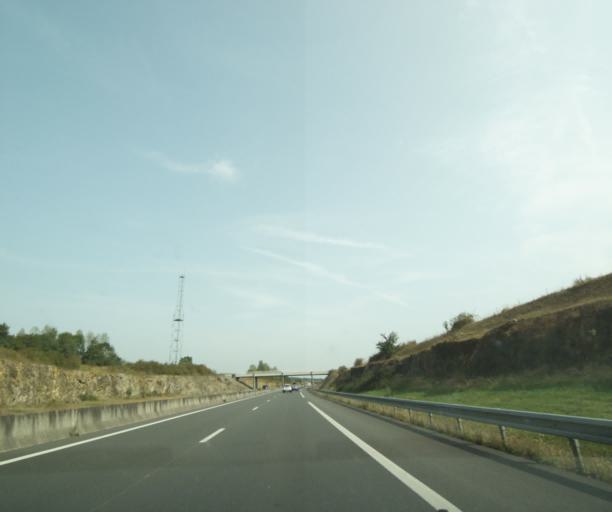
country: FR
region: Pays de la Loire
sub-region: Departement de la Sarthe
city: Arconnay
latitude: 48.3571
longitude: 0.0967
